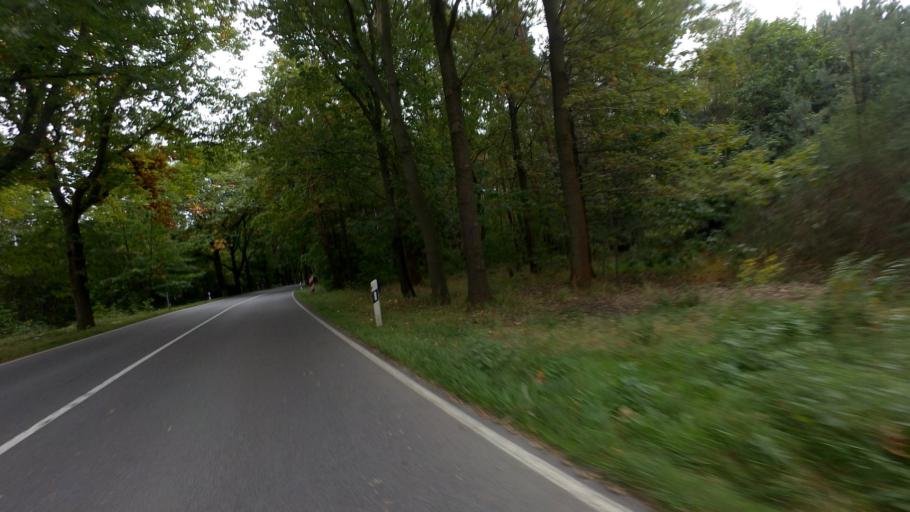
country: DE
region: Saxony
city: Wittichenau
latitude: 51.3909
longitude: 14.2974
